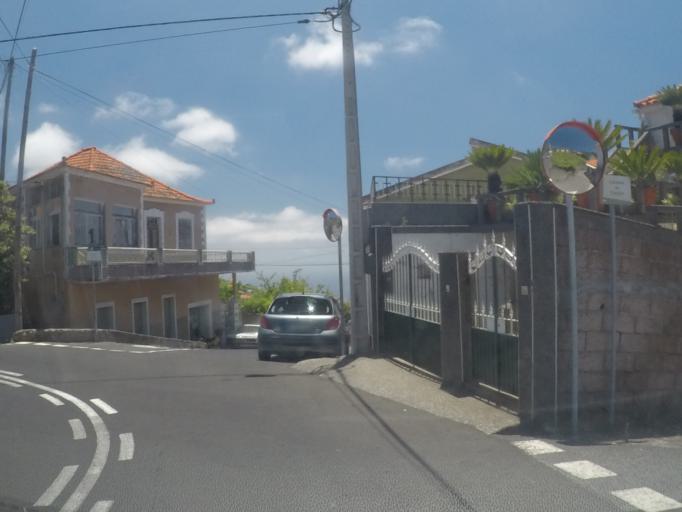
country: PT
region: Madeira
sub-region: Camara de Lobos
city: Curral das Freiras
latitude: 32.6807
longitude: -16.9901
